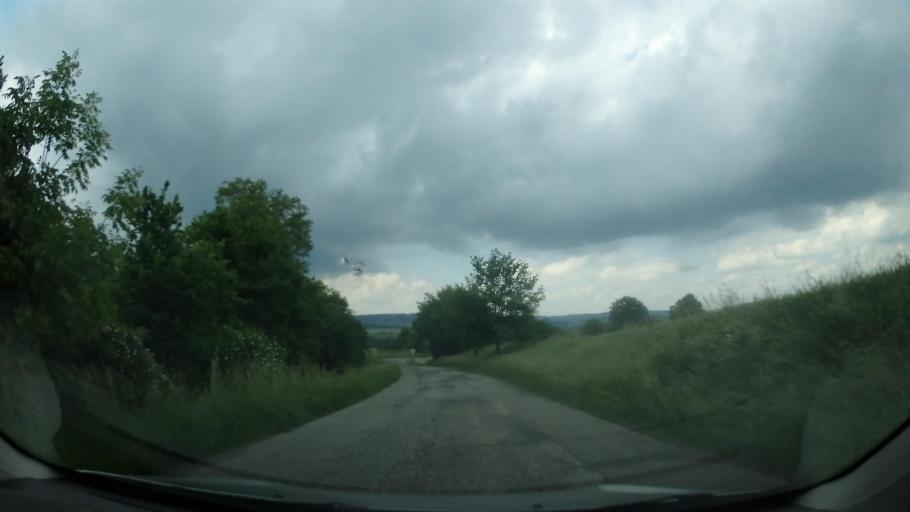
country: CZ
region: South Moravian
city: Doubravice nad Svitavou
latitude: 49.4629
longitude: 16.6050
